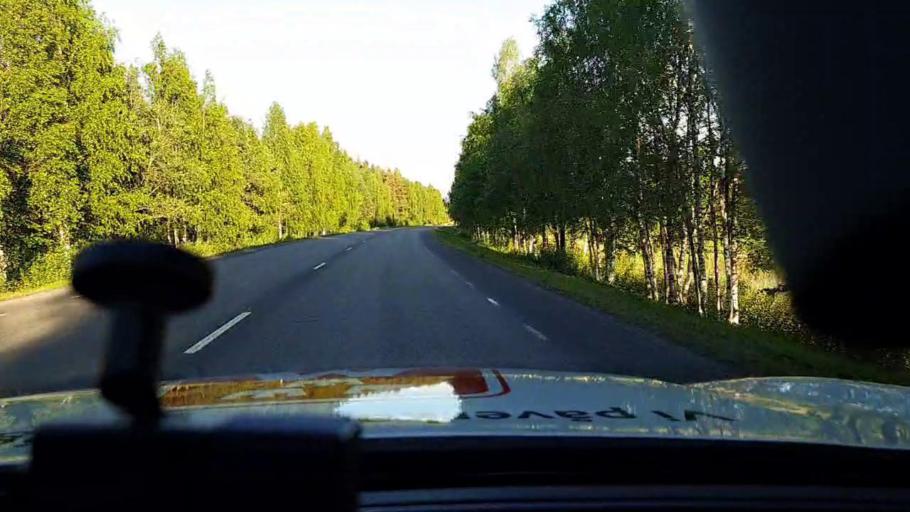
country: SE
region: Norrbotten
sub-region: Lulea Kommun
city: Lulea
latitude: 65.6117
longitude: 22.1625
